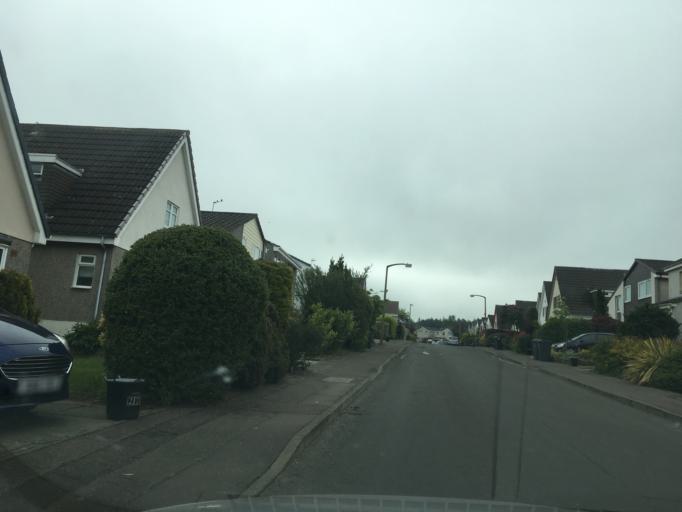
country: GB
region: Scotland
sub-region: Edinburgh
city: Edinburgh
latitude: 55.9065
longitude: -3.2020
